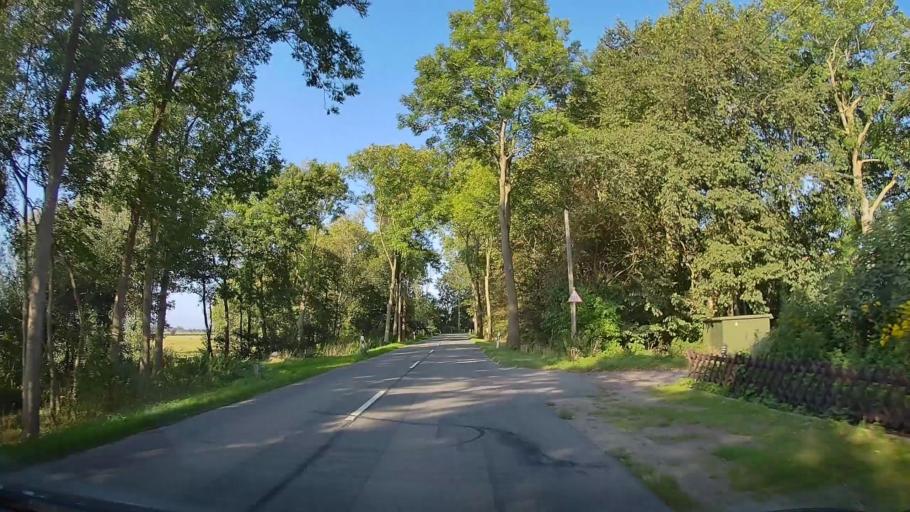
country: DE
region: Lower Saxony
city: Nordholz
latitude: 53.7671
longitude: 8.5690
